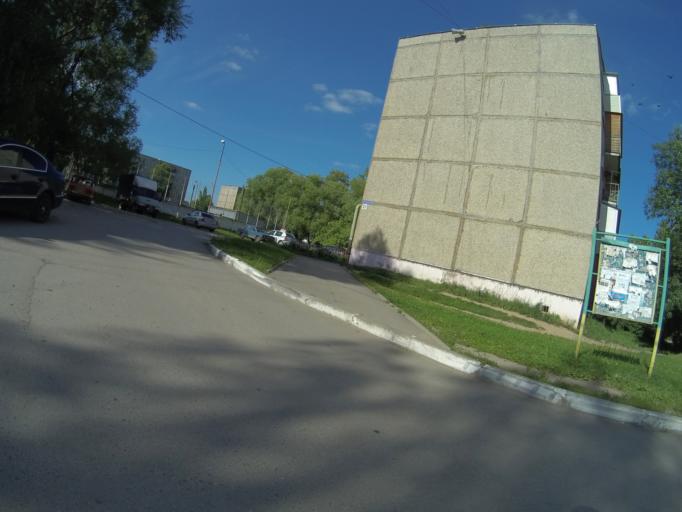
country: RU
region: Vladimir
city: Vorsha
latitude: 56.0967
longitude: 40.1934
